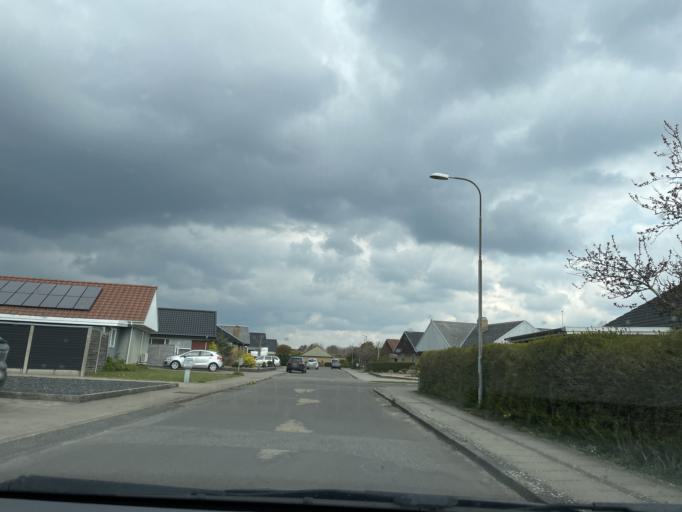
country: DK
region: South Denmark
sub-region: Esbjerg Kommune
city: Esbjerg
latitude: 55.4956
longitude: 8.4270
